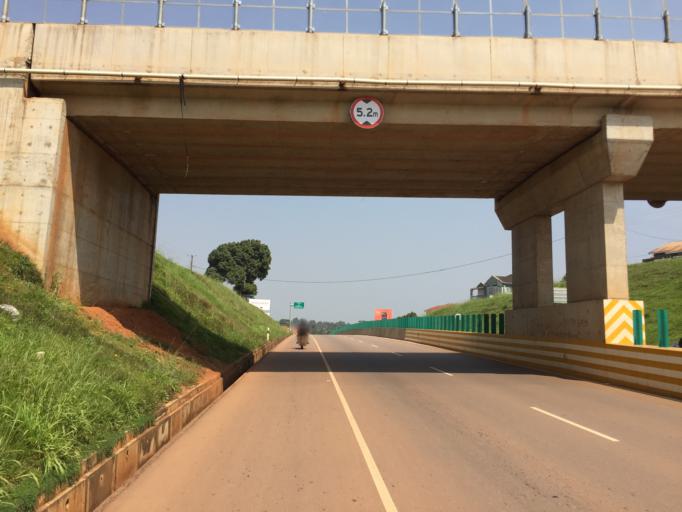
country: UG
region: Central Region
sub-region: Kampala District
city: Kampala
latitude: 0.2385
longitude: 32.6176
